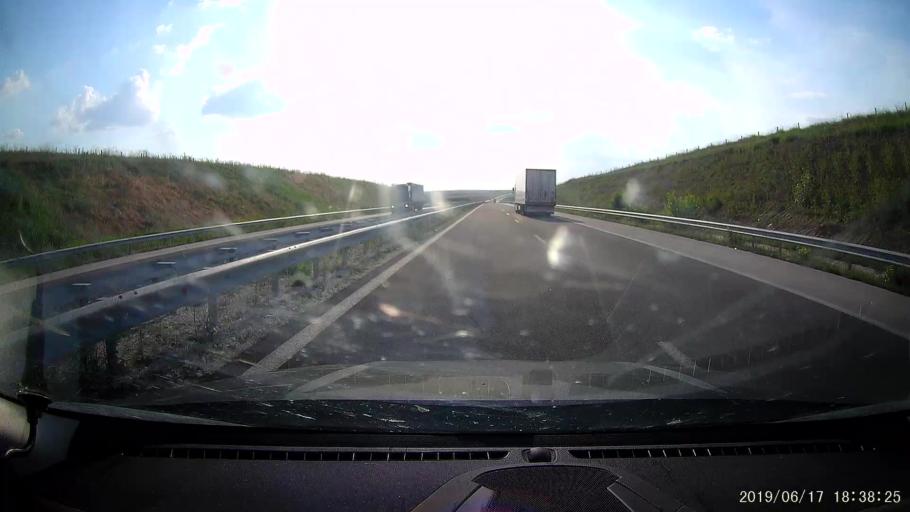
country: BG
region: Stara Zagora
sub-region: Obshtina Chirpan
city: Chirpan
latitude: 42.1368
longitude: 25.3376
